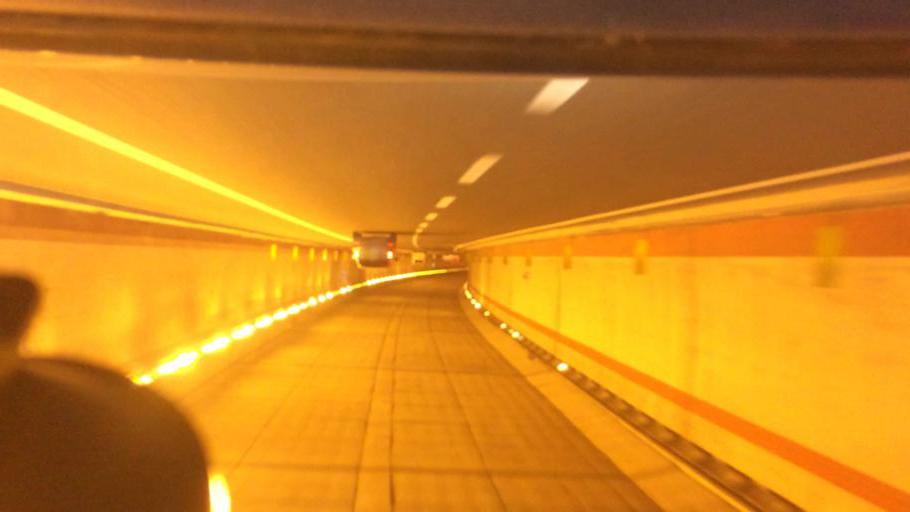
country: IT
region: Lombardy
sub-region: Citta metropolitana di Milano
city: Castano Primo
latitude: 45.5552
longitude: 8.7921
